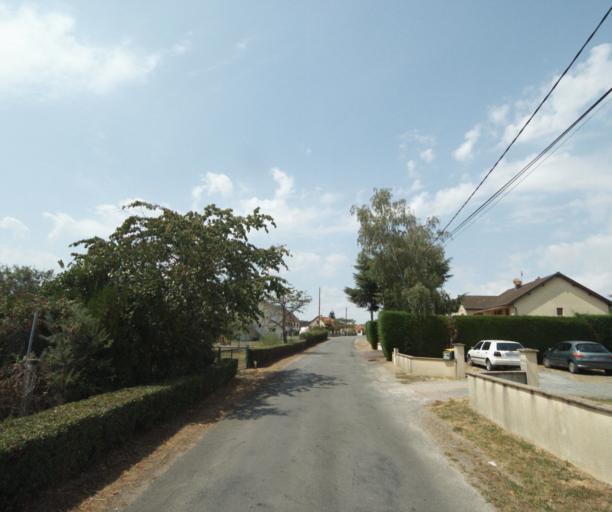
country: FR
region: Bourgogne
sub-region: Departement de Saone-et-Loire
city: Gueugnon
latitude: 46.6030
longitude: 4.0172
